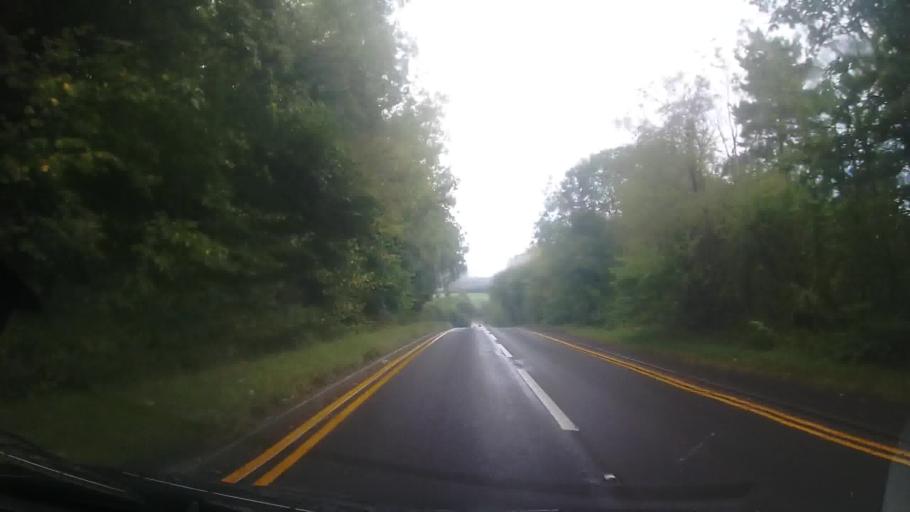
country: GB
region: England
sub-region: Shropshire
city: Much Wenlock
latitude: 52.6066
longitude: -2.5535
